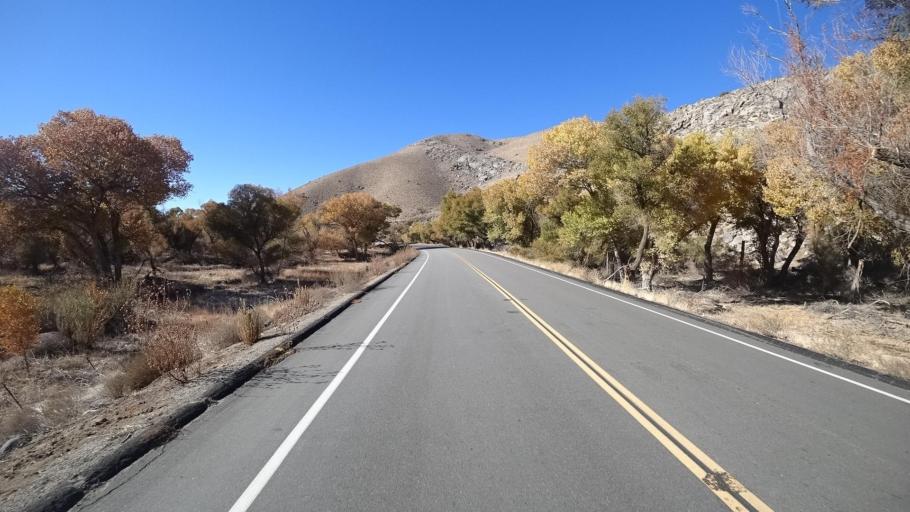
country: US
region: California
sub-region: Kern County
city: Weldon
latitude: 35.6726
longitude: -118.3401
